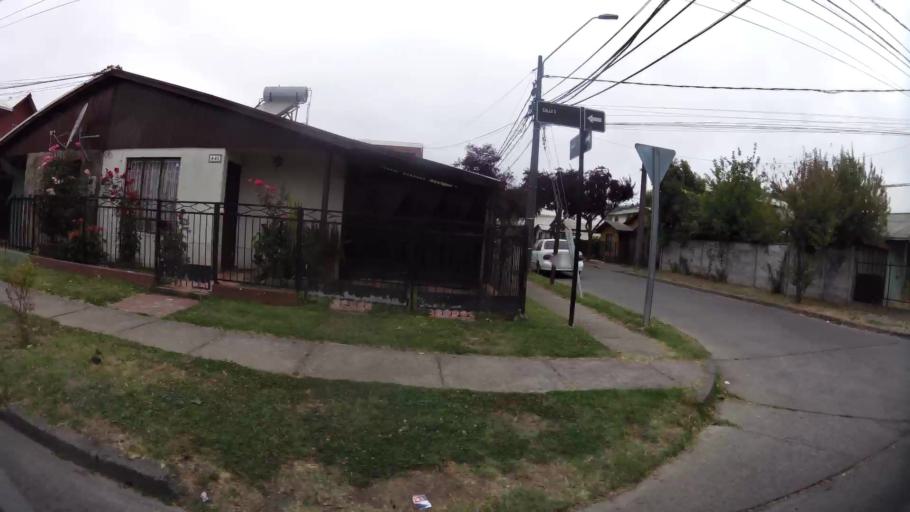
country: CL
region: Biobio
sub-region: Provincia de Concepcion
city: Concepcion
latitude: -36.8285
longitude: -73.0094
